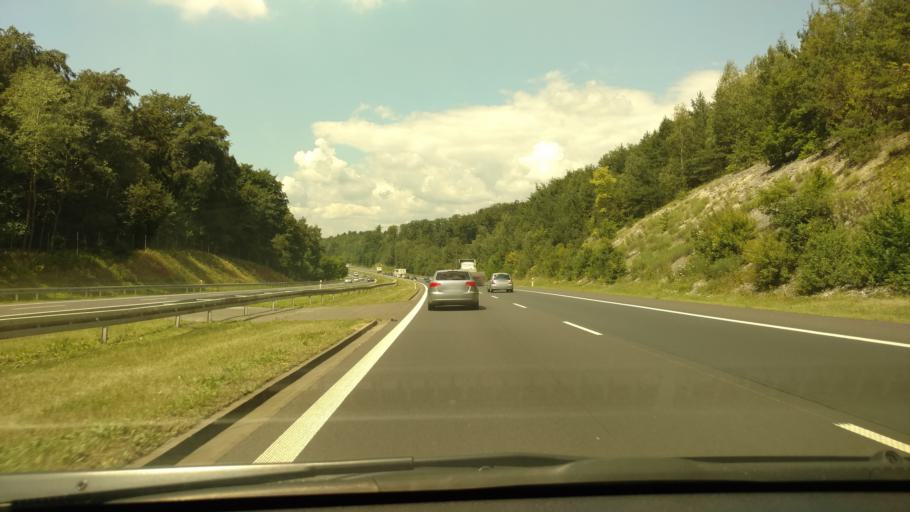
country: PL
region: Lesser Poland Voivodeship
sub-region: Powiat krakowski
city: Czulow
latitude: 50.0922
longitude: 19.6837
